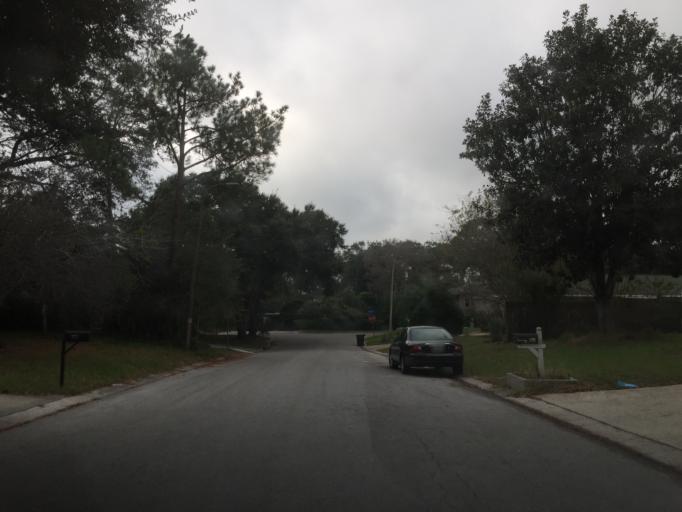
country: US
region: Florida
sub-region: Pinellas County
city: Clearwater
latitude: 27.9535
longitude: -82.7514
